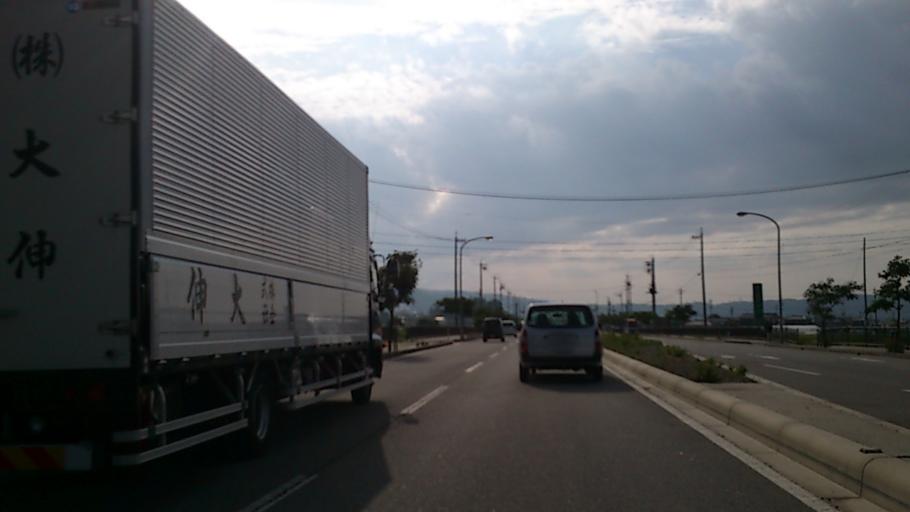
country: JP
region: Nagano
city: Saku
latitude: 36.2343
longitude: 138.4492
